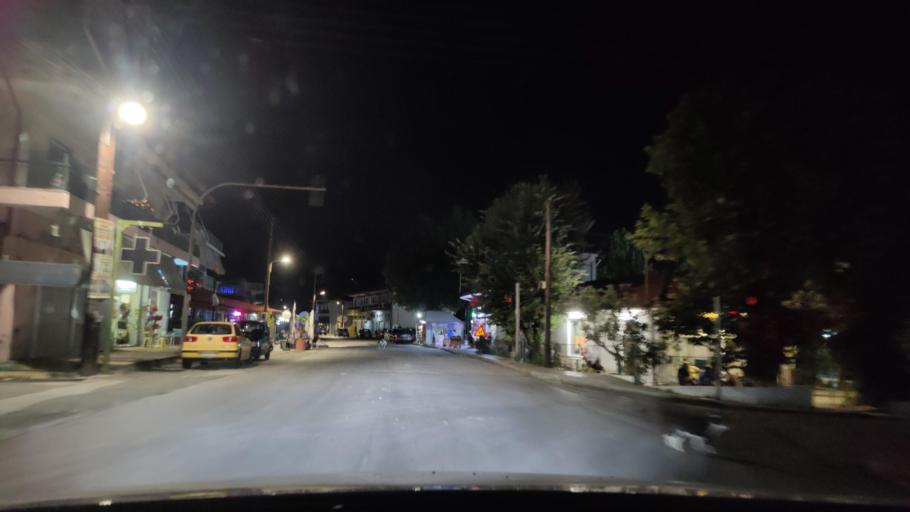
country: GR
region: Central Macedonia
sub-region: Nomos Serron
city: Neo Petritsi
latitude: 41.2652
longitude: 23.2517
